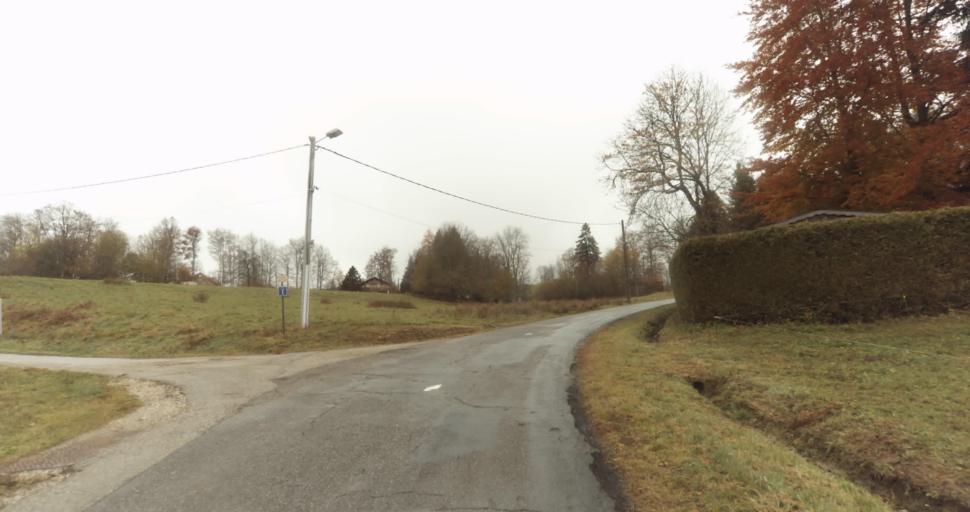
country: FR
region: Rhone-Alpes
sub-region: Departement de la Haute-Savoie
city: Evires
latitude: 46.0620
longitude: 6.2262
